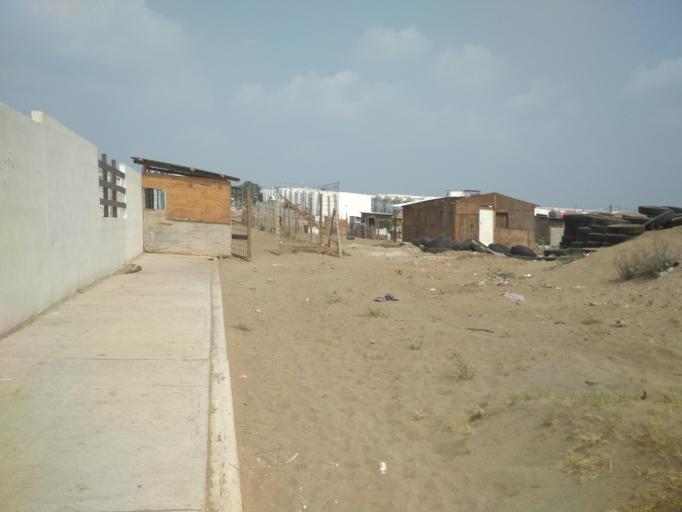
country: MX
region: Veracruz
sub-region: Veracruz
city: Rio Medio [Granja]
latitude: 19.2107
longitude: -96.2106
